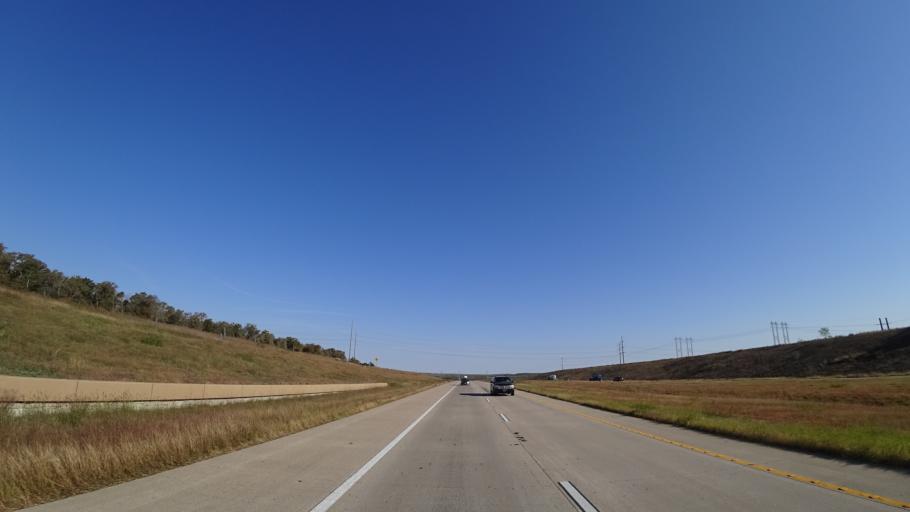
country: US
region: Texas
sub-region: Travis County
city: Hornsby Bend
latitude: 30.2894
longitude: -97.5751
